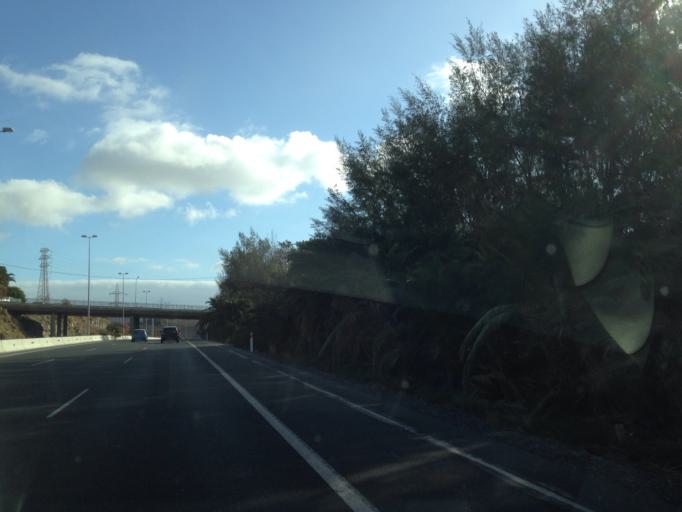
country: ES
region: Canary Islands
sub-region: Provincia de Las Palmas
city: Maspalomas
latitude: 27.7721
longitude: -15.5843
